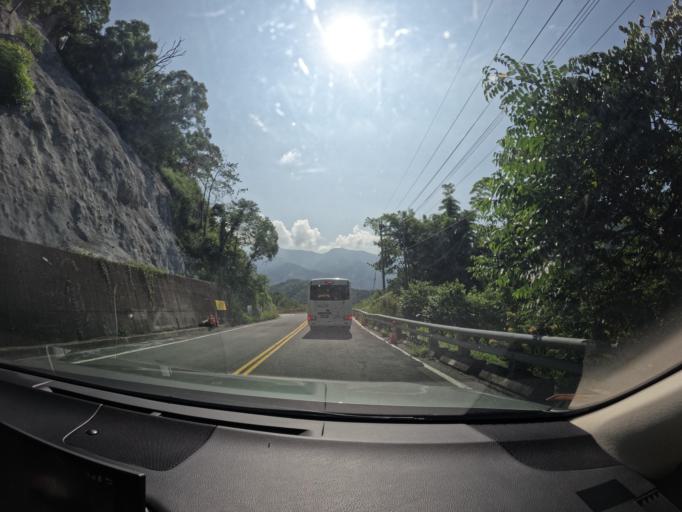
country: TW
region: Taiwan
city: Yujing
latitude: 23.0706
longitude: 120.6414
